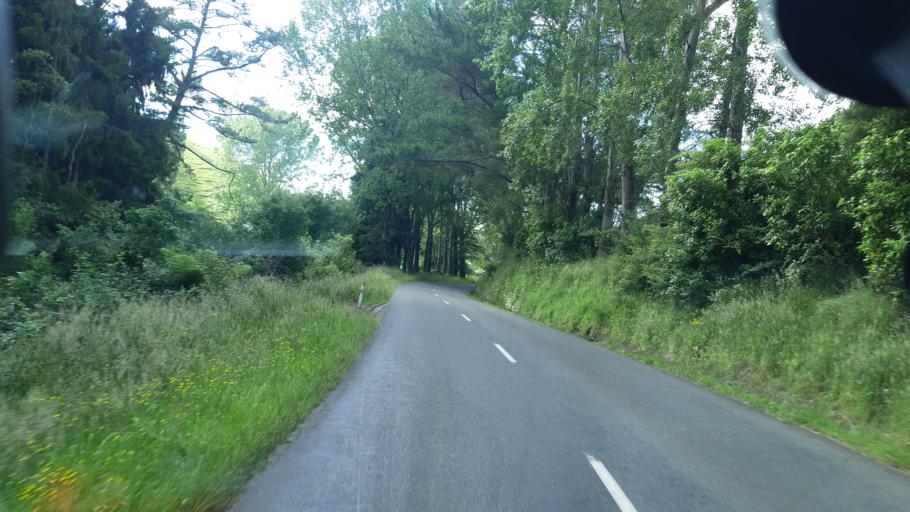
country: NZ
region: Manawatu-Wanganui
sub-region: Rangitikei District
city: Bulls
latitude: -39.9216
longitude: 175.5566
